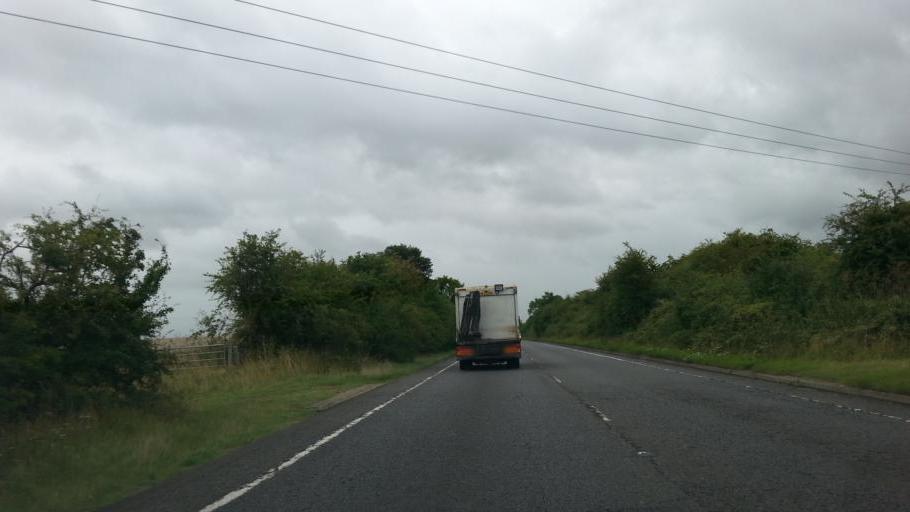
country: GB
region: England
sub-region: Northamptonshire
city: Oundle
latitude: 52.4658
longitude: -0.4600
